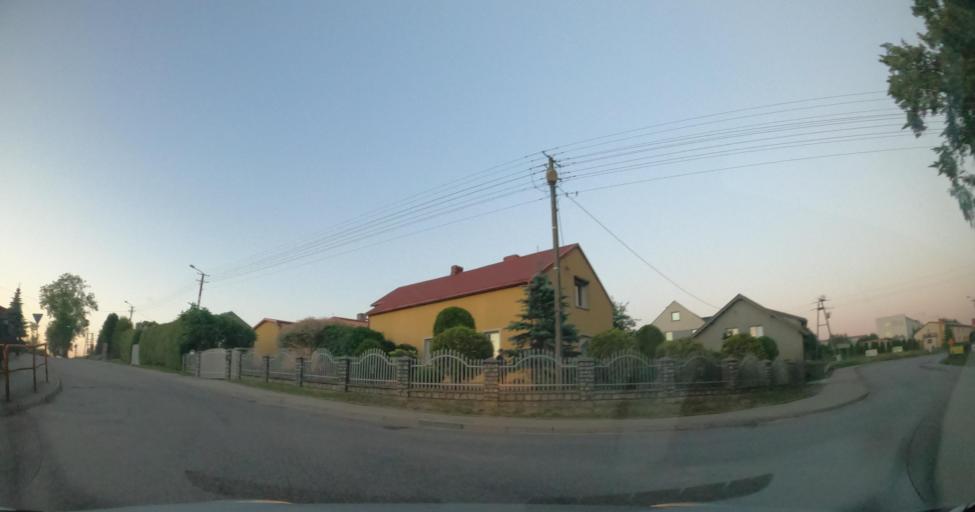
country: PL
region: Pomeranian Voivodeship
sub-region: Powiat wejherowski
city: Szemud
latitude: 54.4625
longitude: 18.1397
